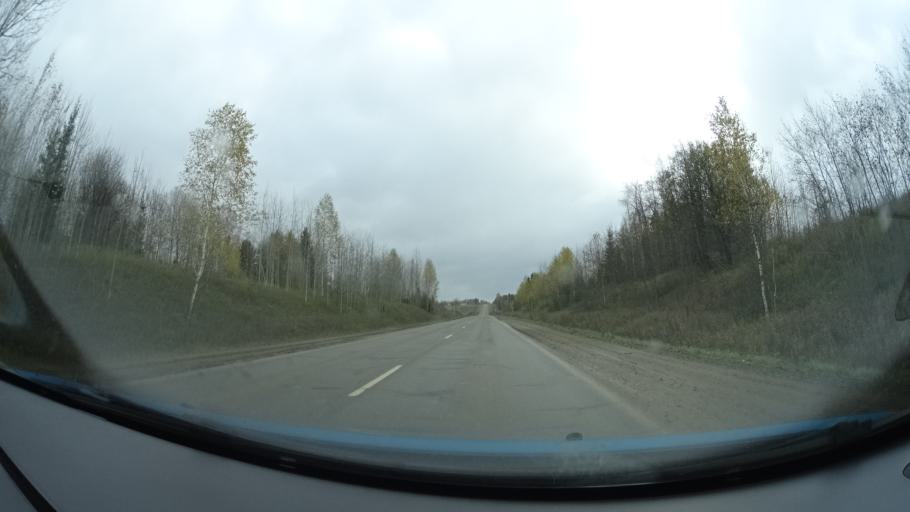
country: RU
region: Perm
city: Chernushka
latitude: 56.7433
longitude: 56.1622
